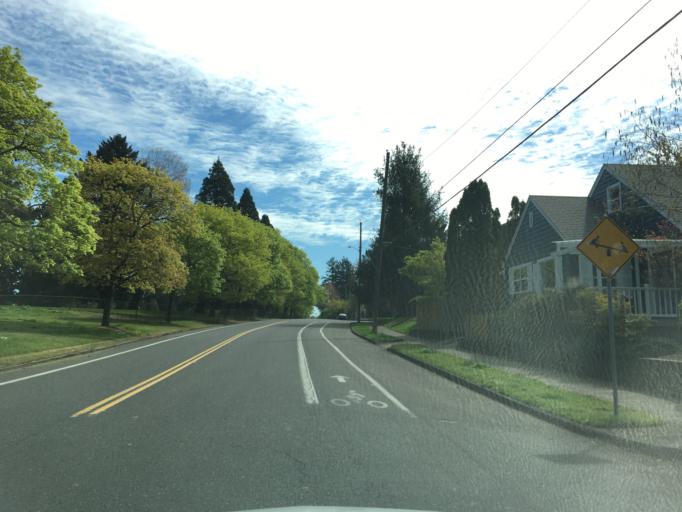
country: US
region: Oregon
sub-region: Multnomah County
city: Lents
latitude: 45.5373
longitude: -122.5969
